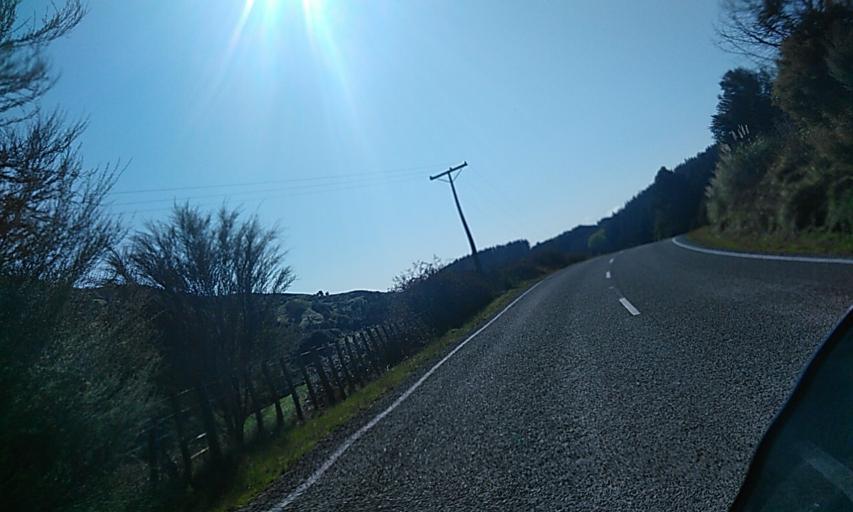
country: NZ
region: Gisborne
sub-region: Gisborne District
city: Gisborne
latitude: -38.5844
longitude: 178.0041
